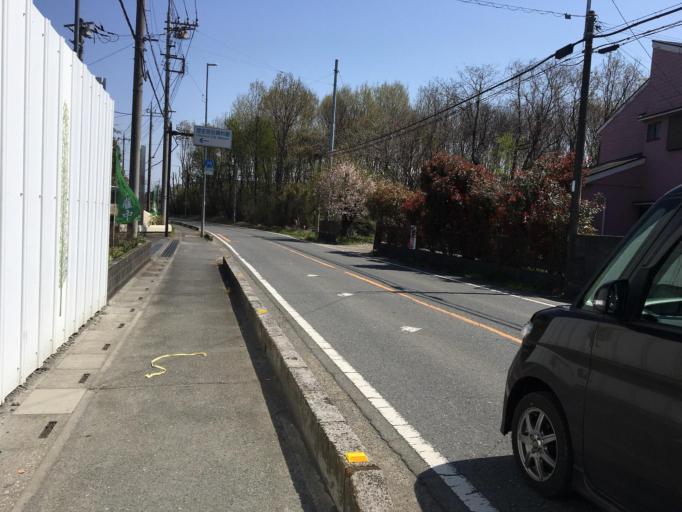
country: JP
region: Saitama
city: Sakado
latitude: 35.9549
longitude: 139.3464
